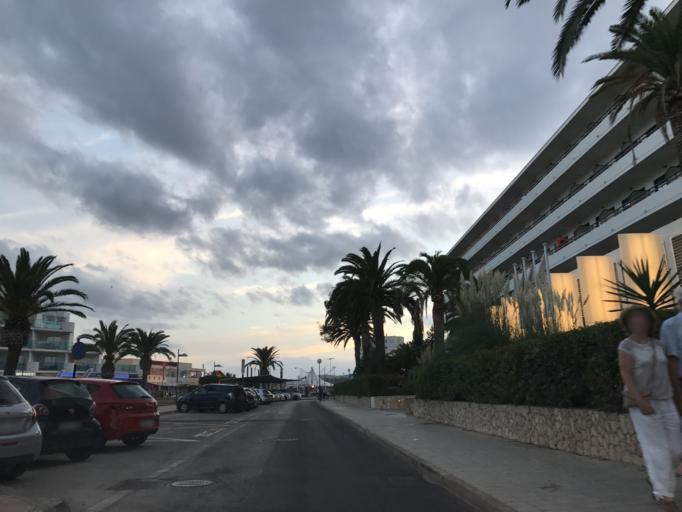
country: ES
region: Balearic Islands
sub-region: Illes Balears
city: Son Servera
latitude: 39.5949
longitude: 3.3826
